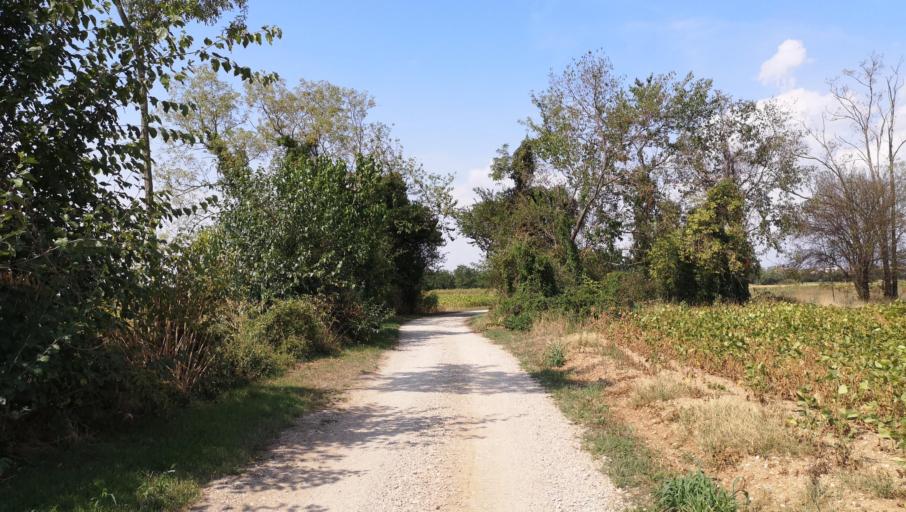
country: IT
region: Friuli Venezia Giulia
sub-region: Provincia di Udine
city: Udine
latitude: 46.0447
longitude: 13.2689
